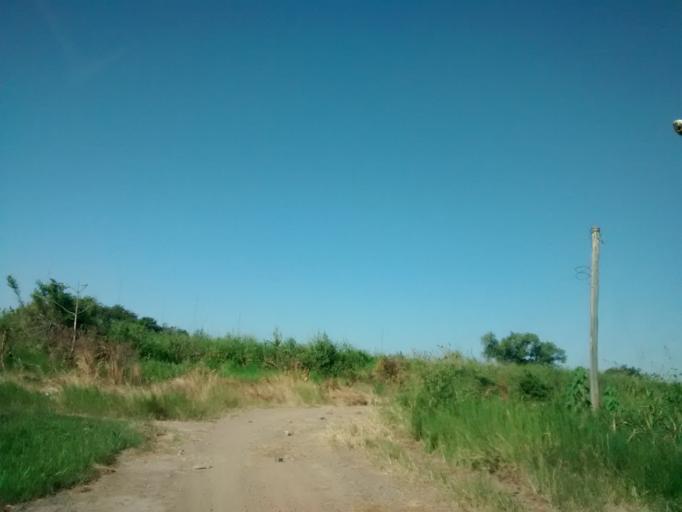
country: AR
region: Chaco
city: Fontana
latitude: -27.4373
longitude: -59.0117
